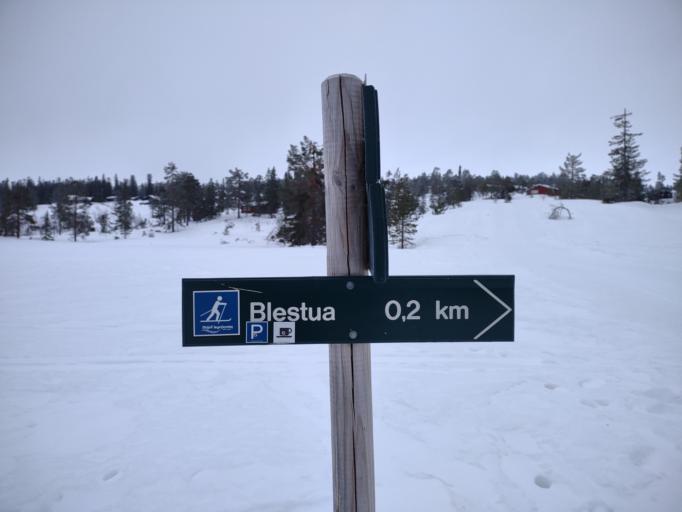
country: NO
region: Buskerud
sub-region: Flesberg
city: Lampeland
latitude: 59.7901
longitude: 9.4208
